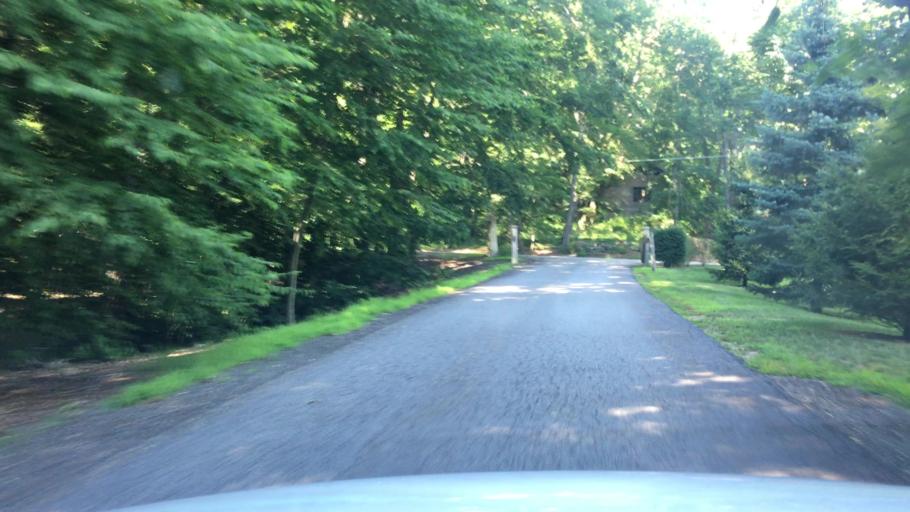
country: US
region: New Hampshire
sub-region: Rockingham County
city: Kensington
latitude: 42.9156
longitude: -70.9359
